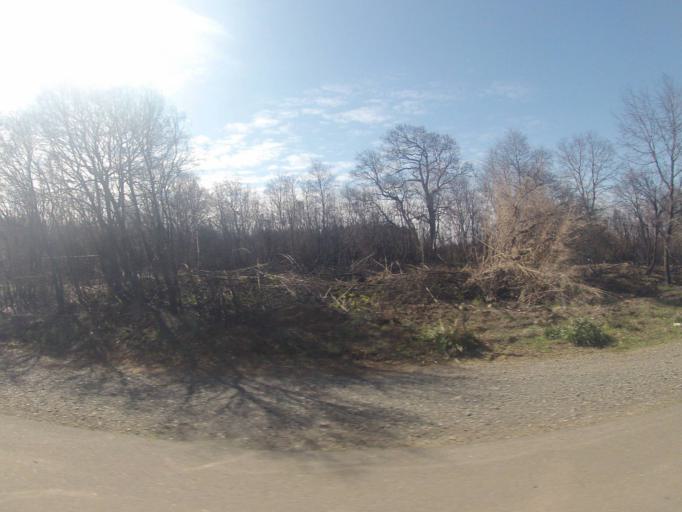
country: CL
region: Araucania
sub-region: Provincia de Malleco
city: Victoria
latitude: -38.1517
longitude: -72.3063
